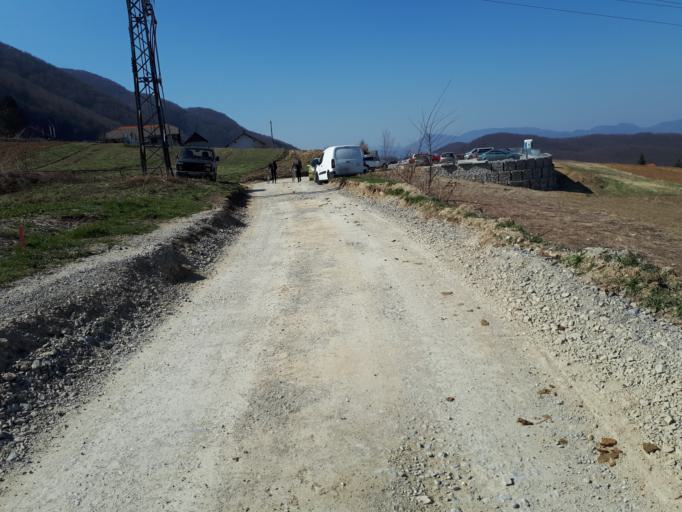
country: HR
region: Varazdinska
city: Ivanec
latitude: 46.1964
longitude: 16.1397
